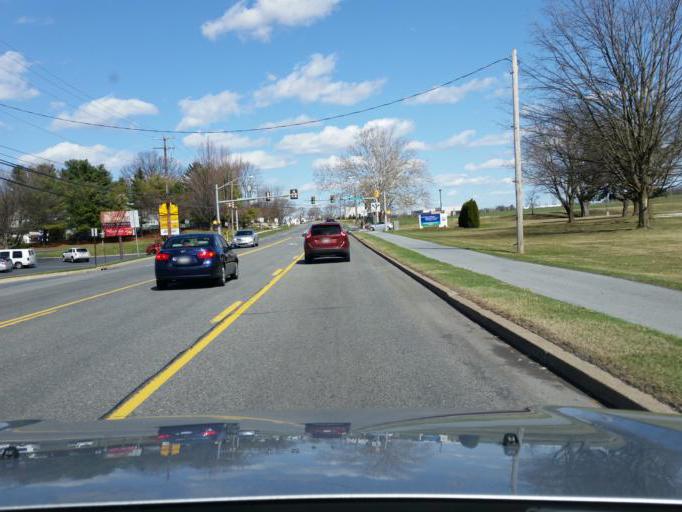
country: US
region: Pennsylvania
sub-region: Dauphin County
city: Hershey
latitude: 40.2685
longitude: -76.6719
